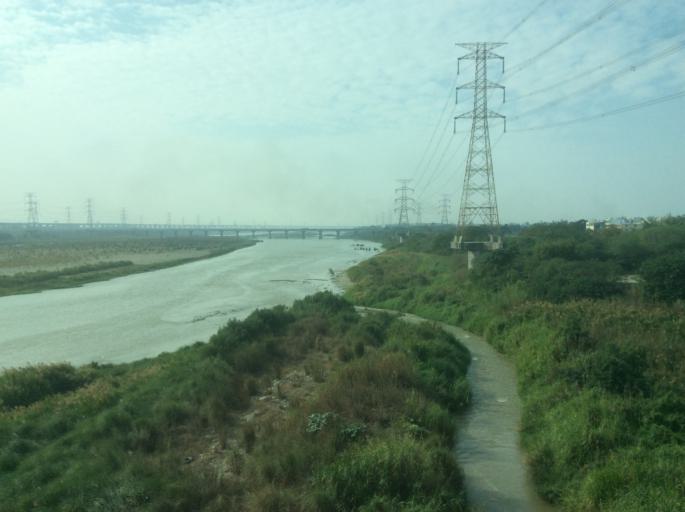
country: TW
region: Taiwan
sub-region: Changhua
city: Chang-hua
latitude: 24.1090
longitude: 120.5777
